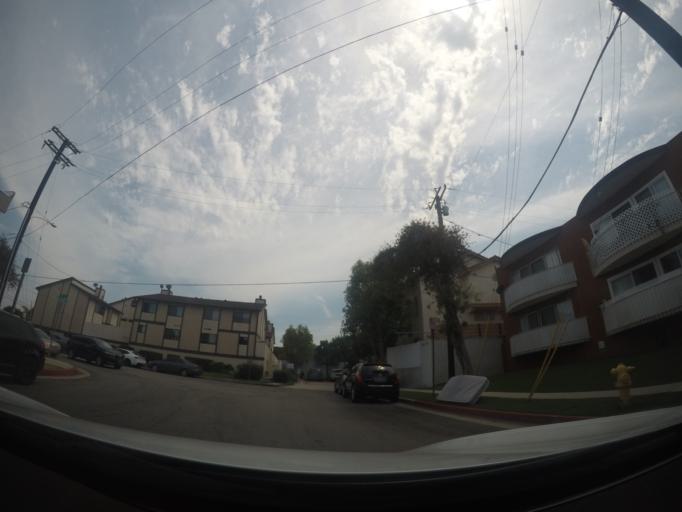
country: US
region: California
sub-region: Los Angeles County
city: Rolling Hills Estates
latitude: 33.8069
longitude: -118.3528
